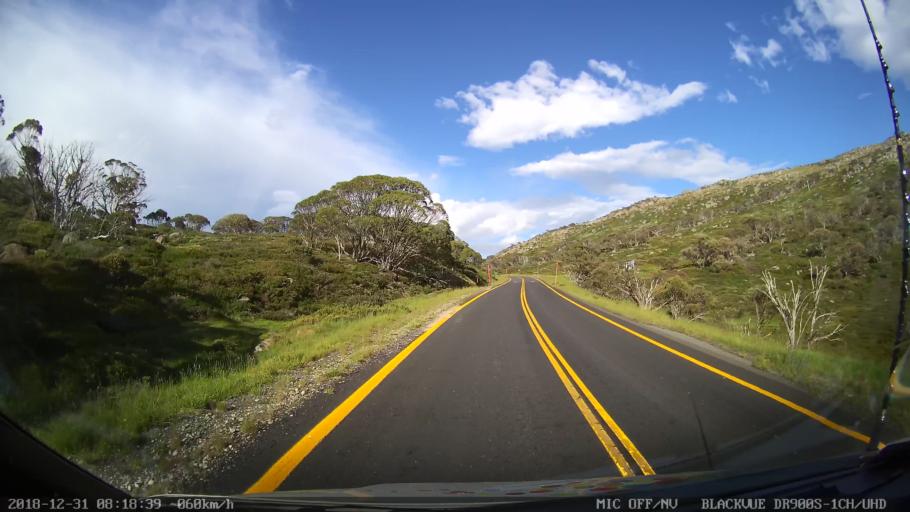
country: AU
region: New South Wales
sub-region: Snowy River
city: Jindabyne
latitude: -36.4158
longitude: 148.3936
